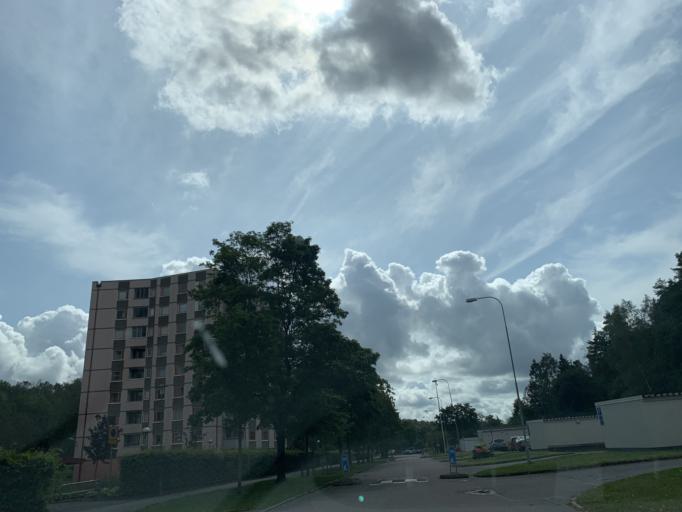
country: SE
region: Vaestra Goetaland
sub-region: Goteborg
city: Eriksbo
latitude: 57.7627
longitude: 12.0606
